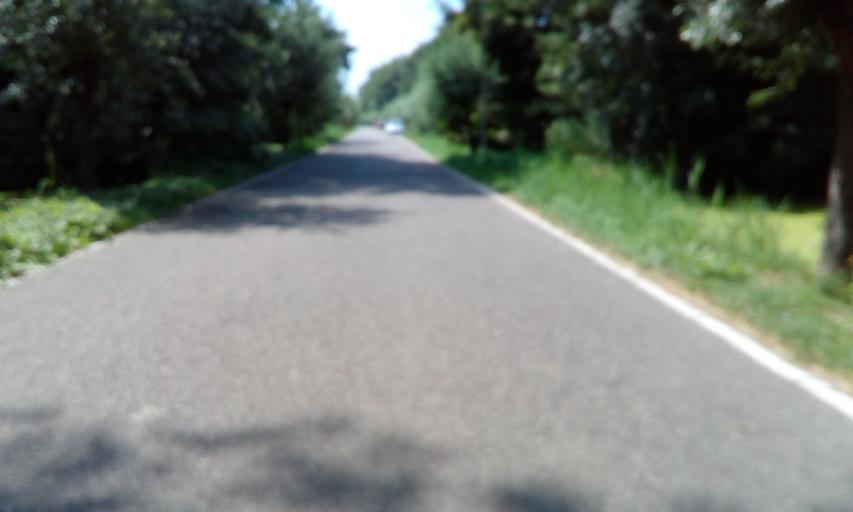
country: NL
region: South Holland
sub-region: Gemeente Capelle aan den IJssel
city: Capelle aan den IJssel
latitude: 51.9389
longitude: 4.5907
